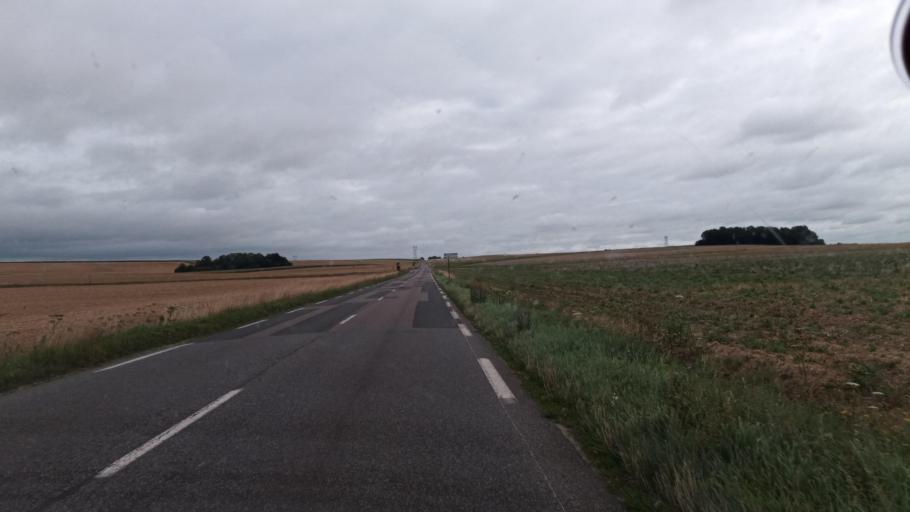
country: FR
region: Ile-de-France
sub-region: Departement de Seine-et-Marne
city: Voulx
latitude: 48.3188
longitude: 2.9507
